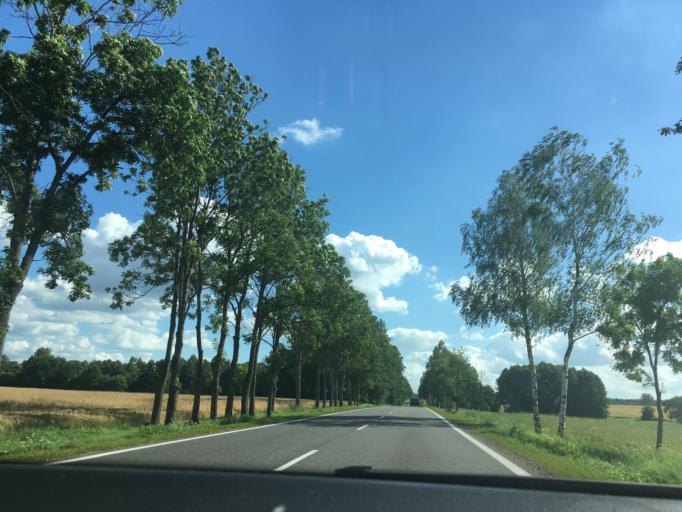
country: PL
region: Podlasie
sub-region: Powiat sokolski
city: Janow
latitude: 53.3819
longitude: 23.1113
